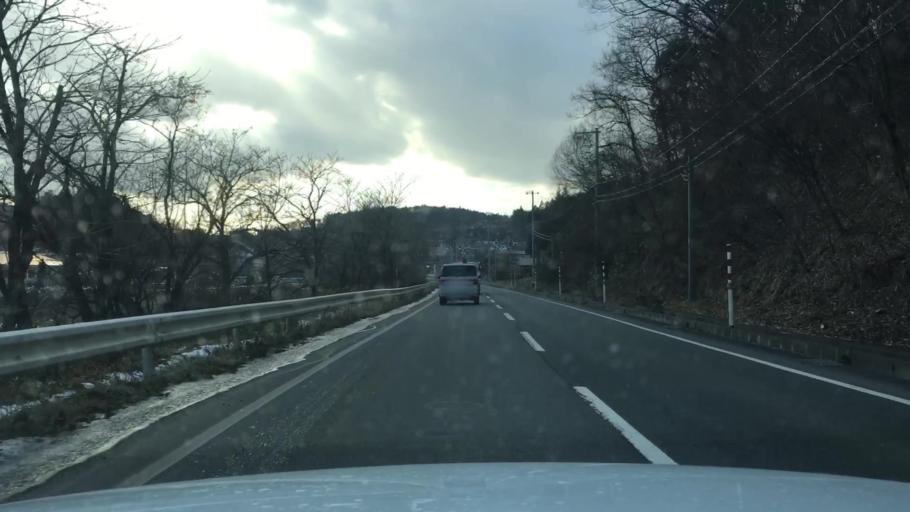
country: JP
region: Iwate
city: Morioka-shi
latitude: 39.6755
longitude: 141.2183
